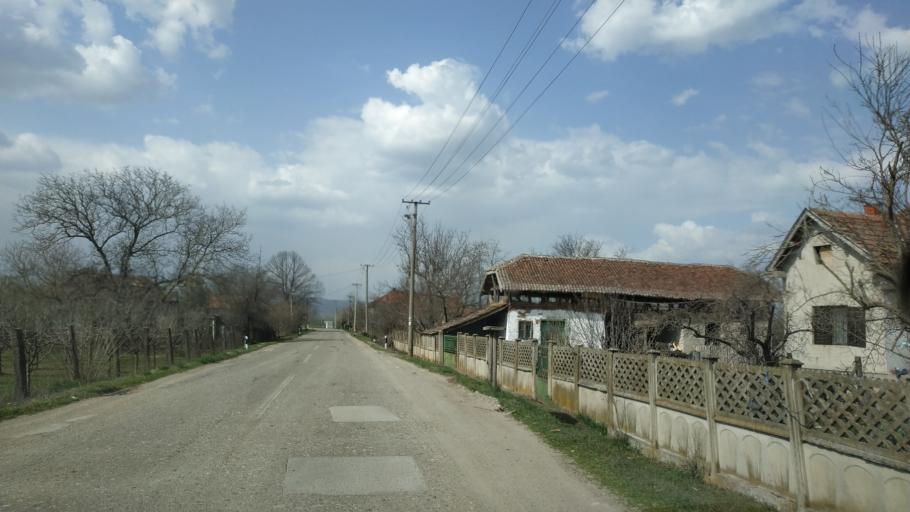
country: RS
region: Central Serbia
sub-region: Nisavski Okrug
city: Razanj
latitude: 43.5866
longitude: 21.5694
